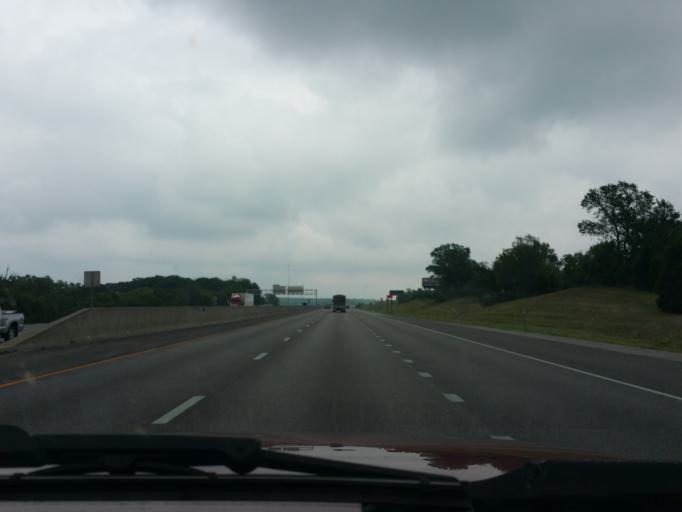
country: US
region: Kansas
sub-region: Wyandotte County
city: Edwardsville
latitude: 39.1062
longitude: -94.8293
